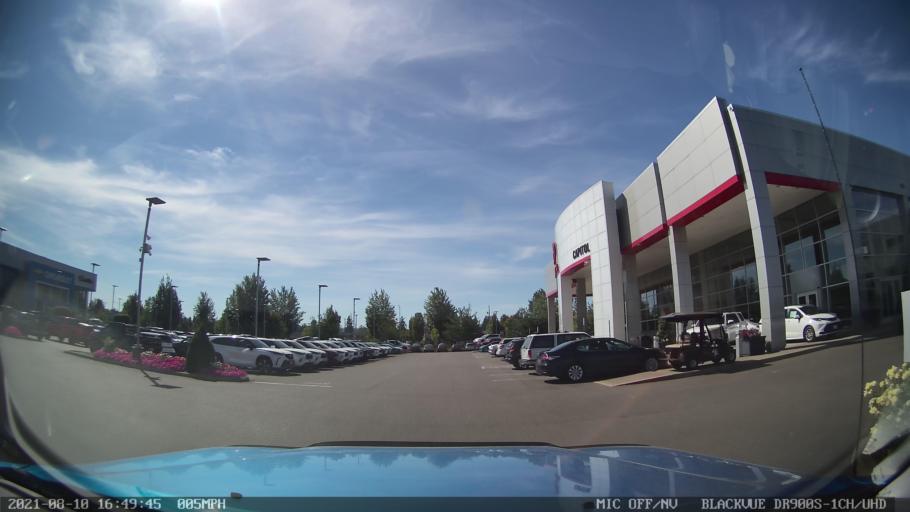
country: US
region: Oregon
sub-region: Marion County
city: Keizer
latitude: 44.9690
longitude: -123.0258
